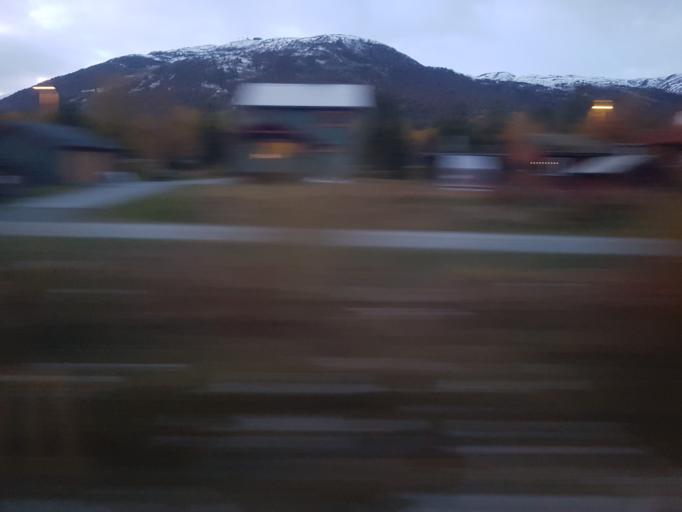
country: NO
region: Sor-Trondelag
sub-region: Oppdal
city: Oppdal
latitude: 62.5989
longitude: 9.7142
